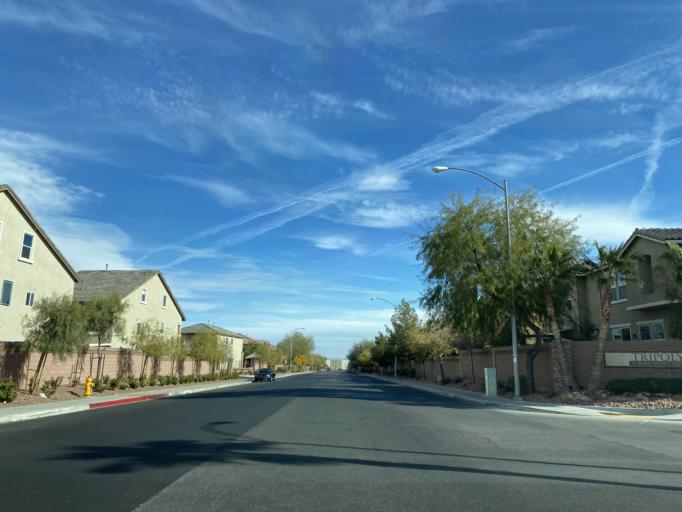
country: US
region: Nevada
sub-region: Clark County
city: Enterprise
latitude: 36.0599
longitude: -115.2306
